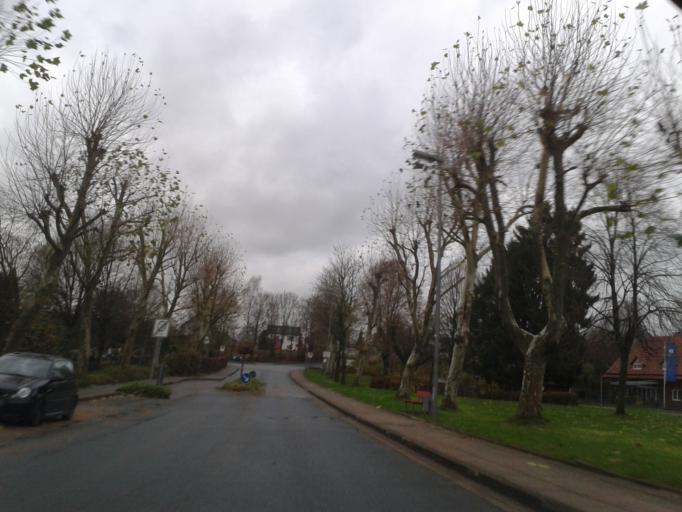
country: DE
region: North Rhine-Westphalia
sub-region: Regierungsbezirk Detmold
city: Blomberg
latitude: 51.9438
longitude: 9.1019
